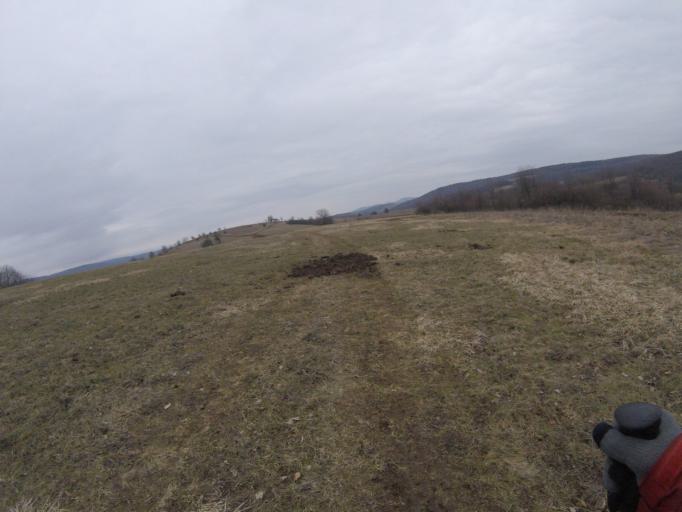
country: HU
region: Borsod-Abauj-Zemplen
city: Rudabanya
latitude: 48.4657
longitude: 20.6043
